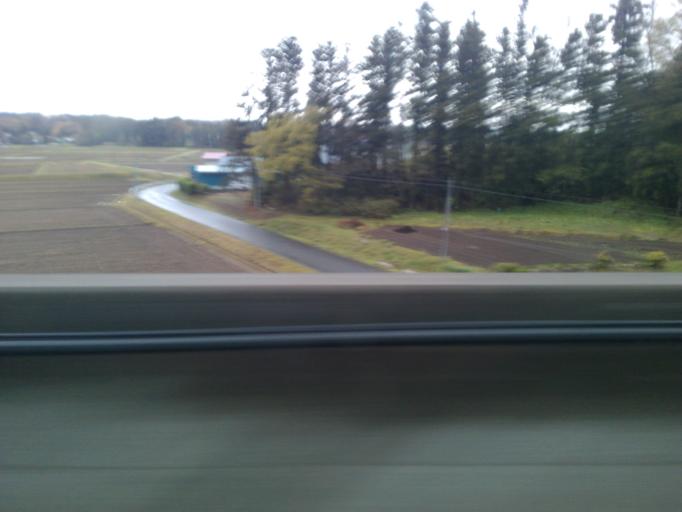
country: JP
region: Miyagi
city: Furukawa
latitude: 38.6233
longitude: 140.9989
